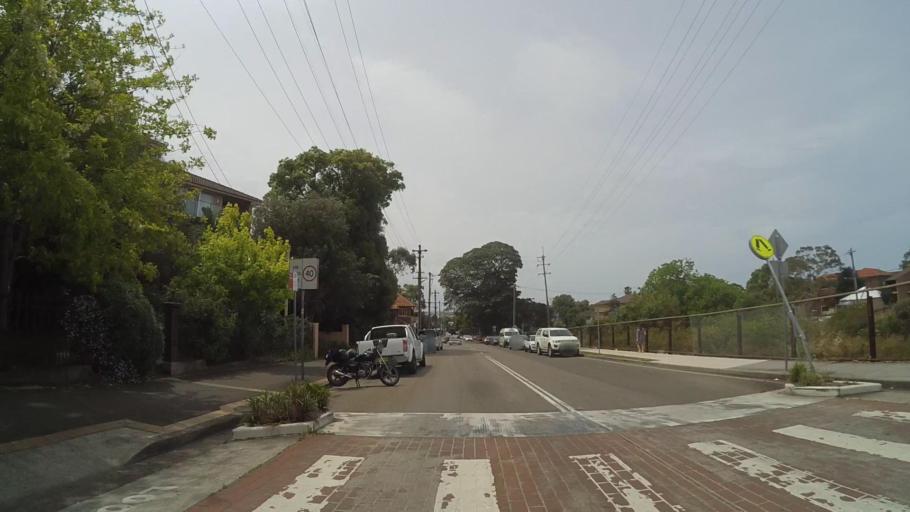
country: AU
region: New South Wales
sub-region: Rockdale
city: Arncliffe
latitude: -33.9387
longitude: 151.1459
